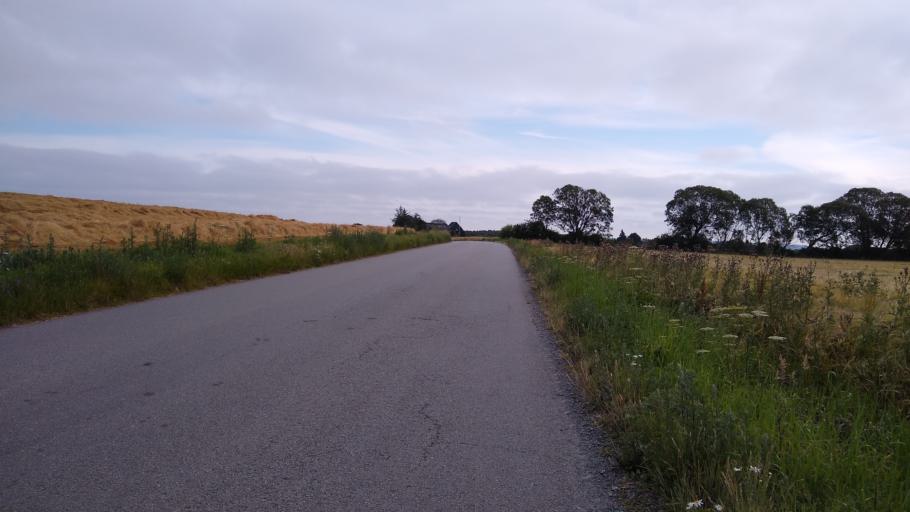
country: DK
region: South Denmark
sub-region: Vejle Kommune
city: Brejning
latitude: 55.6463
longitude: 9.7115
